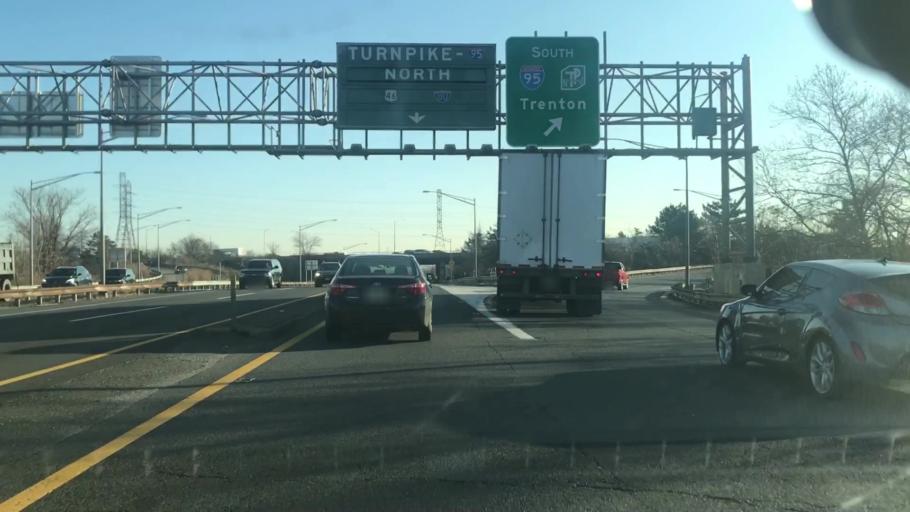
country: US
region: New Jersey
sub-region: Hudson County
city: Kearny
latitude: 40.7548
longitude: -74.1204
